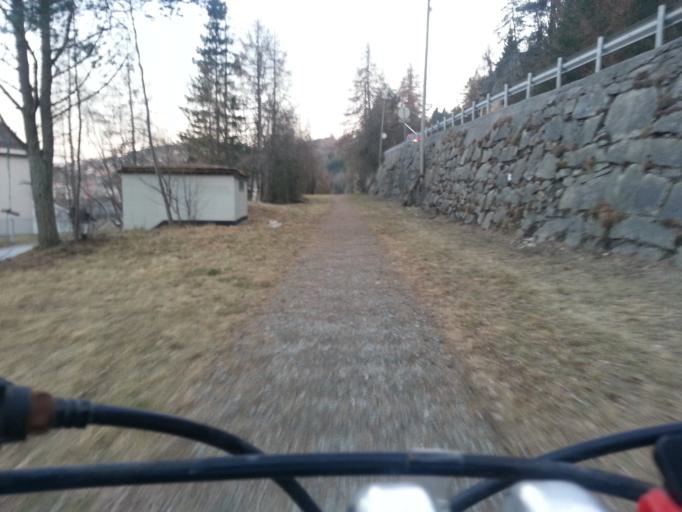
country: NO
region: Sor-Trondelag
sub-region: Trondheim
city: Trondheim
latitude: 63.4376
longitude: 10.3491
